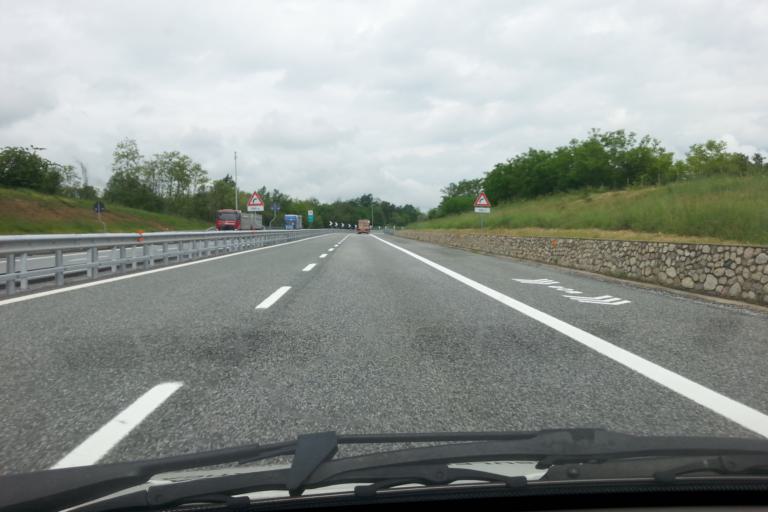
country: IT
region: Piedmont
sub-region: Provincia di Cuneo
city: Lesegno
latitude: 44.3968
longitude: 7.9803
